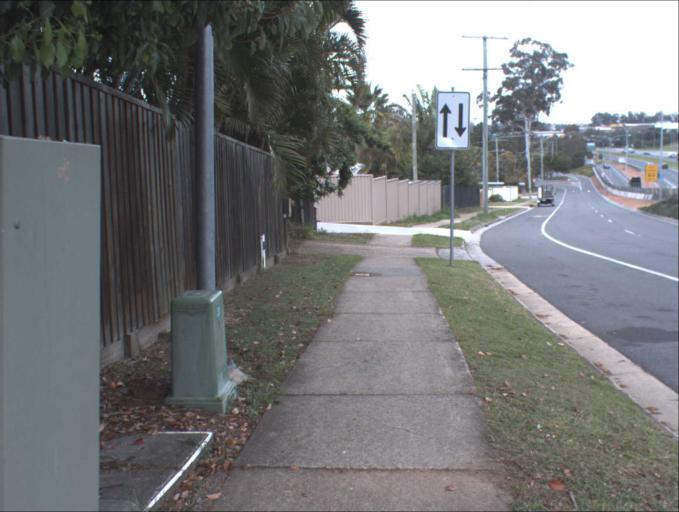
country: AU
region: Queensland
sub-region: Brisbane
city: Sunnybank Hills
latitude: -27.6550
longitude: 153.0405
